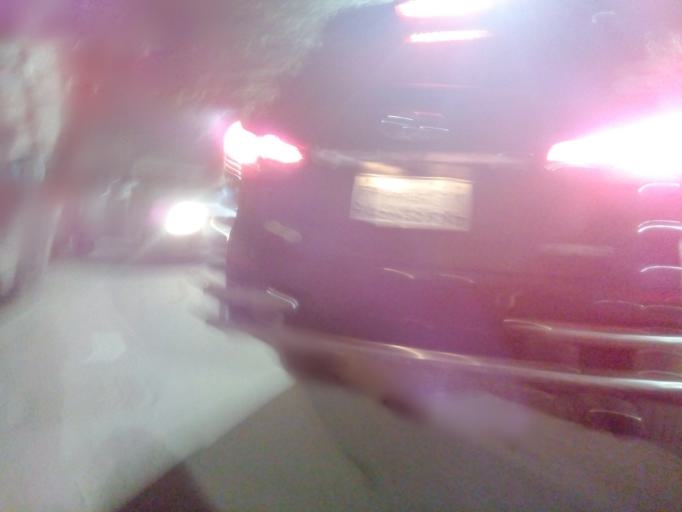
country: BD
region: Dhaka
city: Paltan
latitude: 23.7495
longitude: 90.4231
